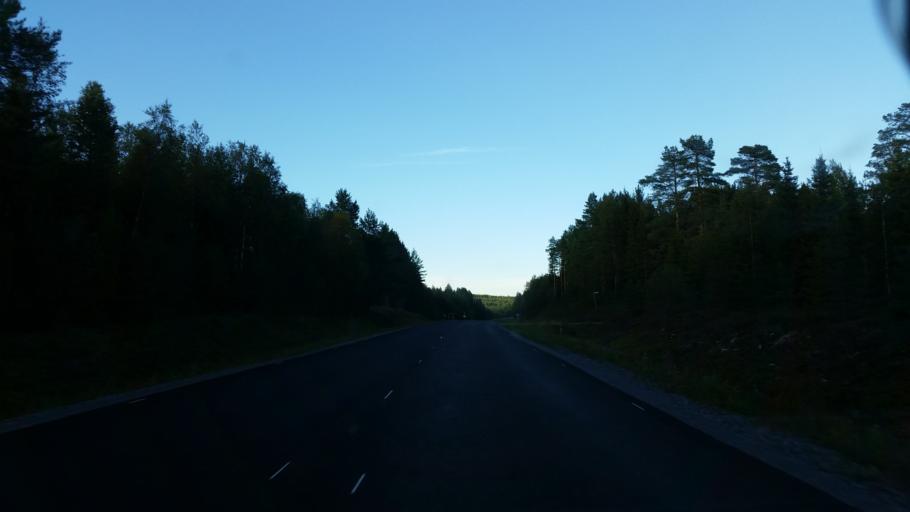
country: SE
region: Vaesterbotten
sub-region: Dorotea Kommun
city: Dorotea
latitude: 64.2936
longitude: 16.5362
